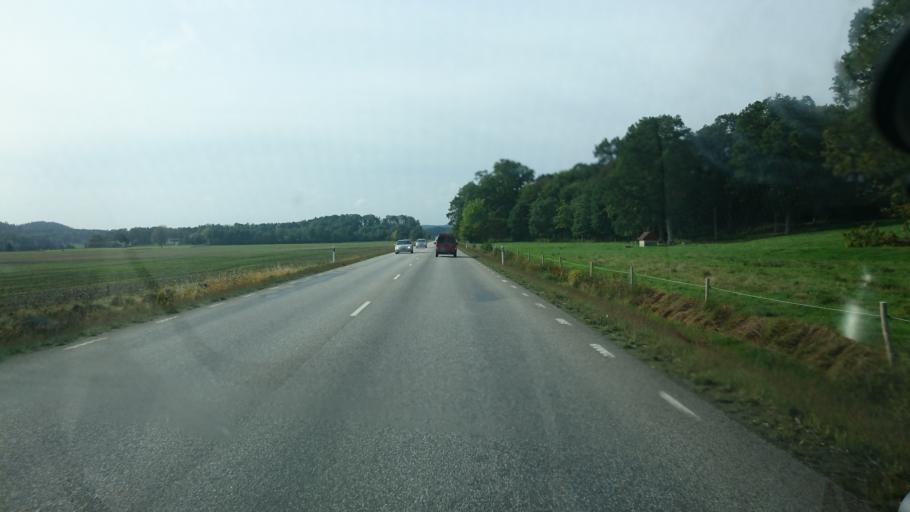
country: SE
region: Vaestra Goetaland
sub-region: Alingsas Kommun
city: Sollebrunn
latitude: 58.1090
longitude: 12.5219
